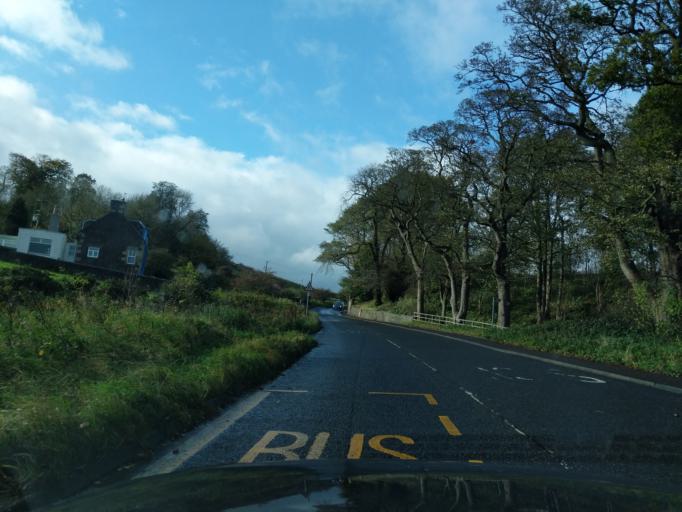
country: GB
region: Scotland
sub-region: Edinburgh
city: Ratho
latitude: 55.9288
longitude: -3.3858
